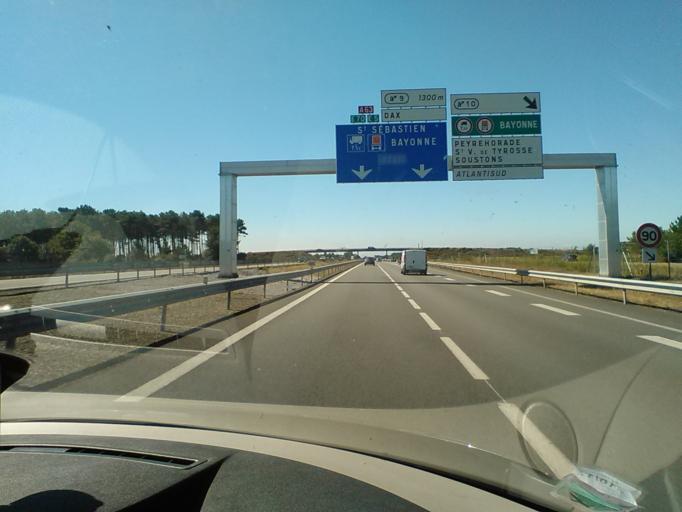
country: FR
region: Aquitaine
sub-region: Departement des Landes
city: Saint-Geours-de-Maremne
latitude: 43.7149
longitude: -1.2280
